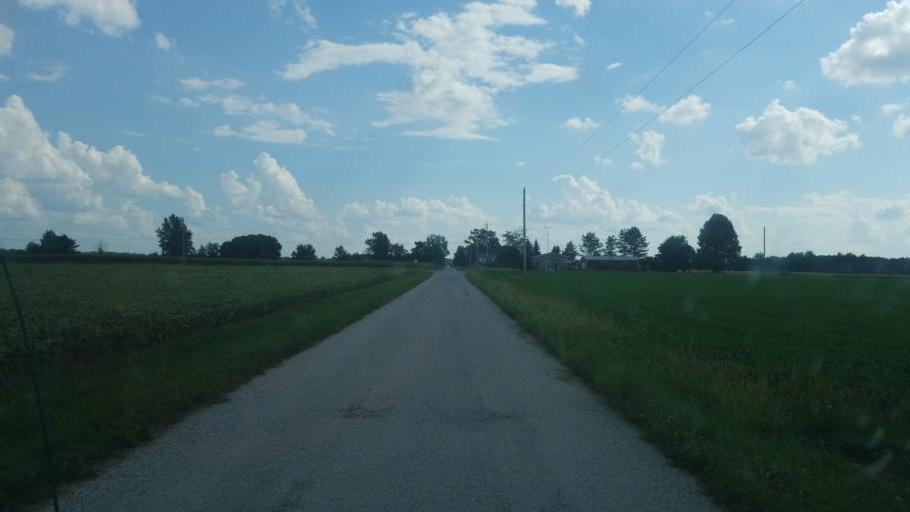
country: US
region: Ohio
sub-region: Huron County
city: Willard
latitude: 40.9832
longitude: -82.8160
